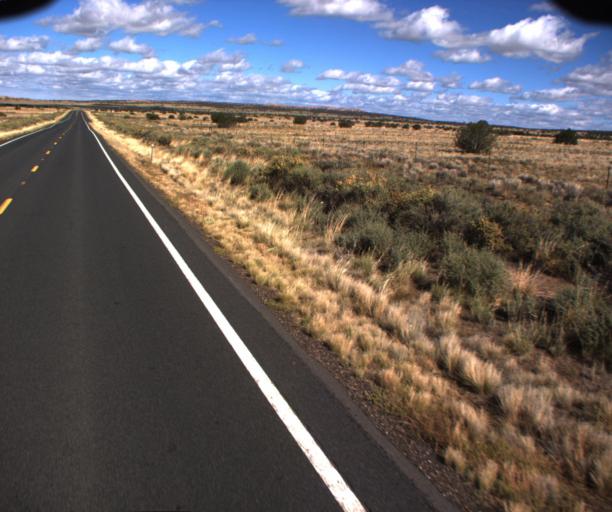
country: US
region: Arizona
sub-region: Apache County
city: Houck
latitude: 35.0399
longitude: -109.2682
